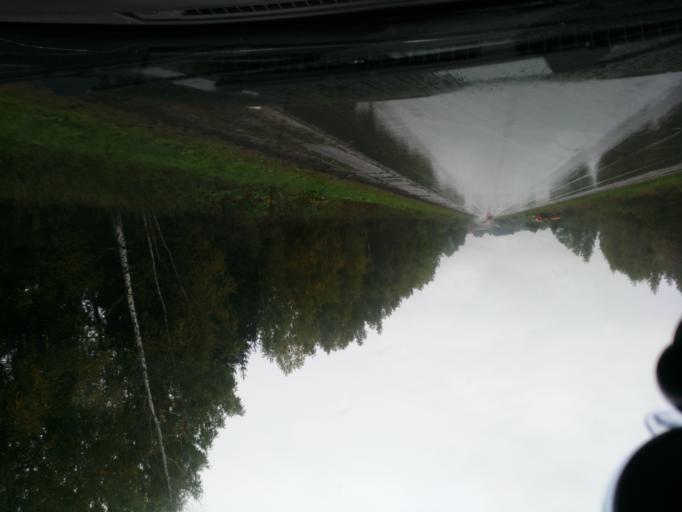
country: RU
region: Perm
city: Osa
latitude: 57.3616
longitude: 55.6022
